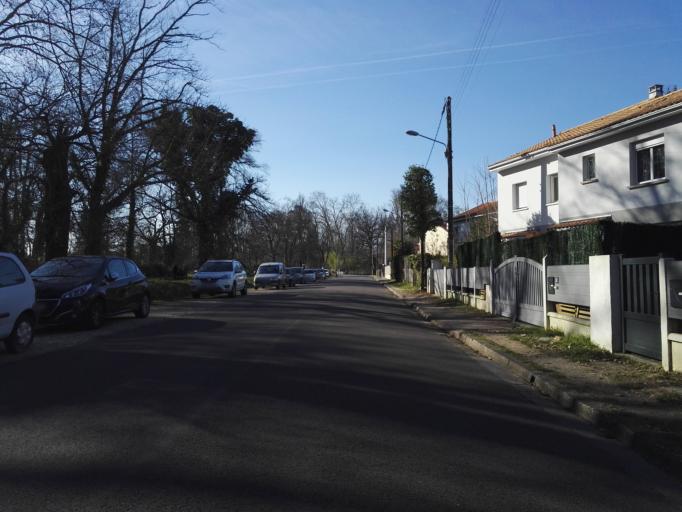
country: FR
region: Aquitaine
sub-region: Departement de la Gironde
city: Merignac
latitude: 44.8256
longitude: -0.6354
